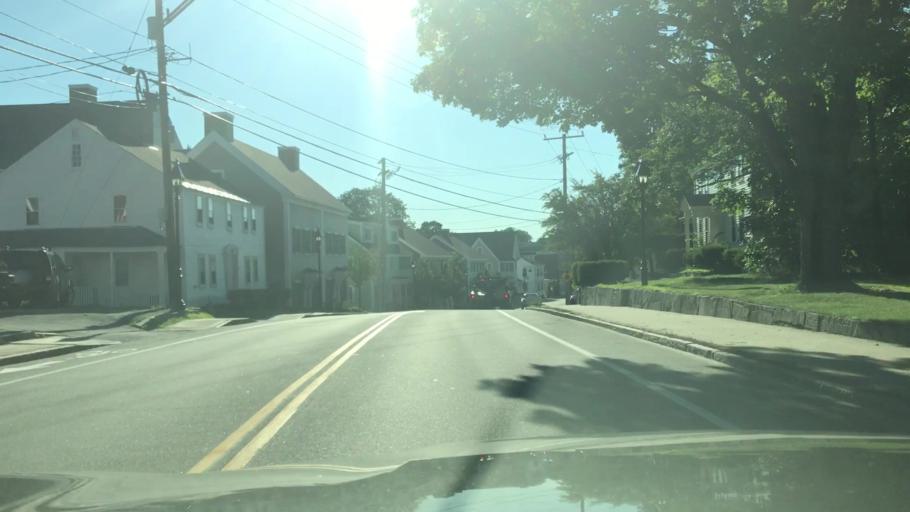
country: US
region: New Hampshire
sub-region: Strafford County
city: Durham
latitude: 43.1333
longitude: -70.9231
